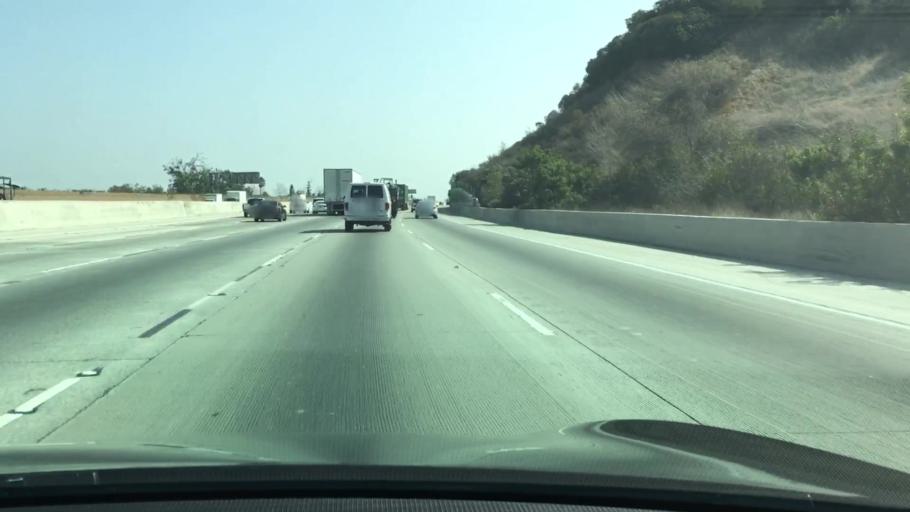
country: US
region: California
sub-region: Los Angeles County
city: Avocado Heights
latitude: 34.0272
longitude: -117.9982
